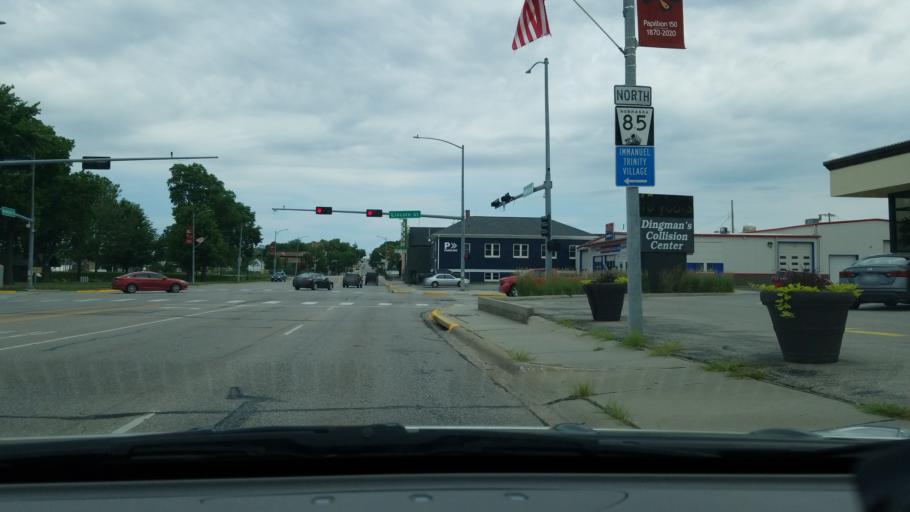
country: US
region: Nebraska
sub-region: Sarpy County
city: Papillion
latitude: 41.1540
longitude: -96.0429
